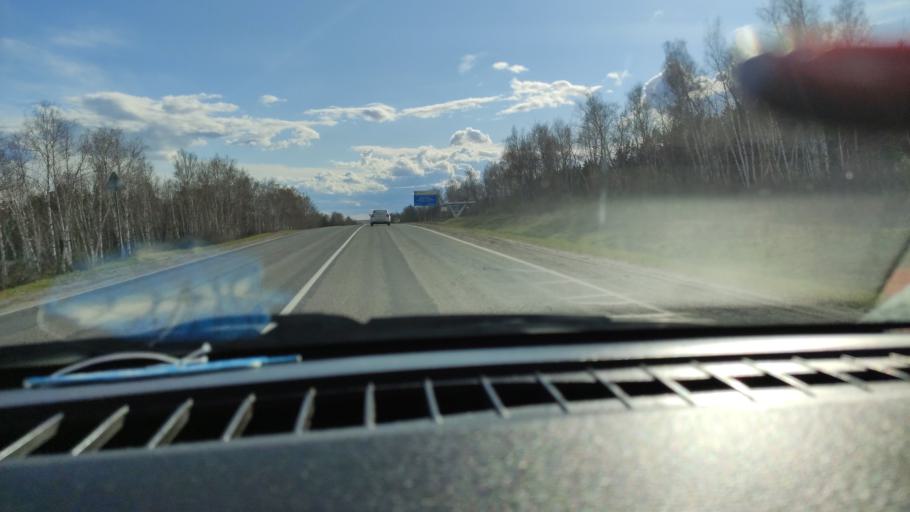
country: RU
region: Saratov
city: Sennoy
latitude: 52.1160
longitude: 46.8380
